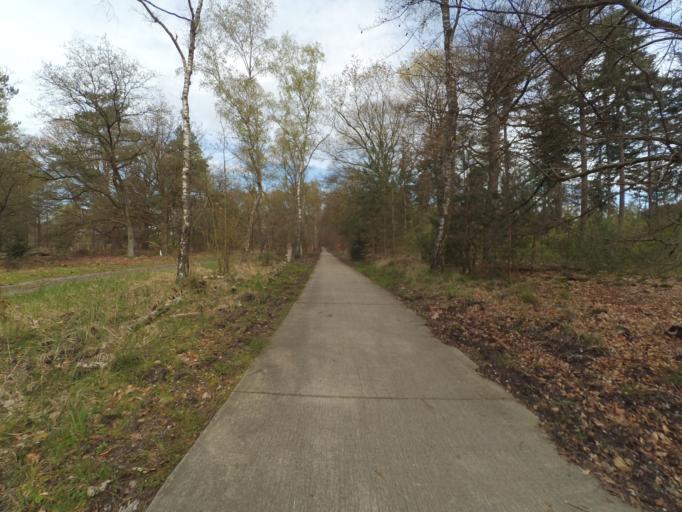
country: NL
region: Gelderland
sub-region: Gemeente Nunspeet
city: Nunspeet
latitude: 52.3400
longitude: 5.7778
